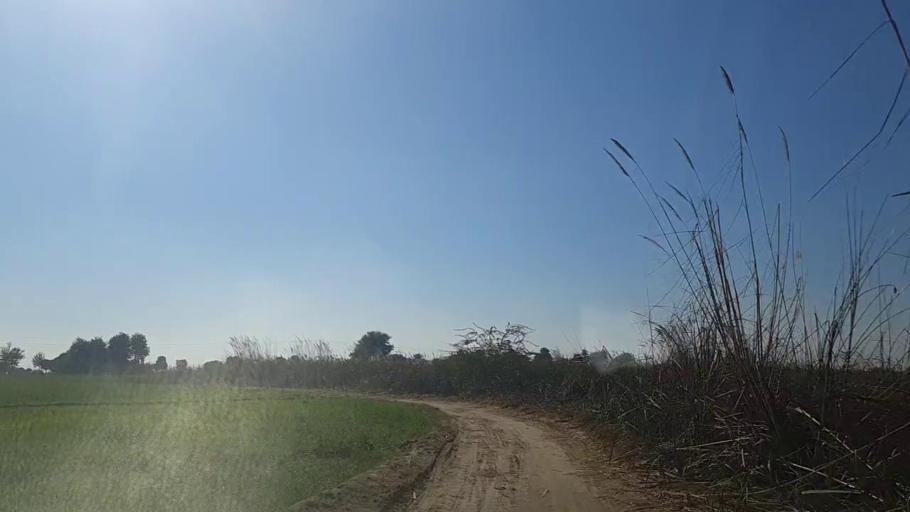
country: PK
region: Sindh
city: Khadro
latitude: 26.1591
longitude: 68.8279
